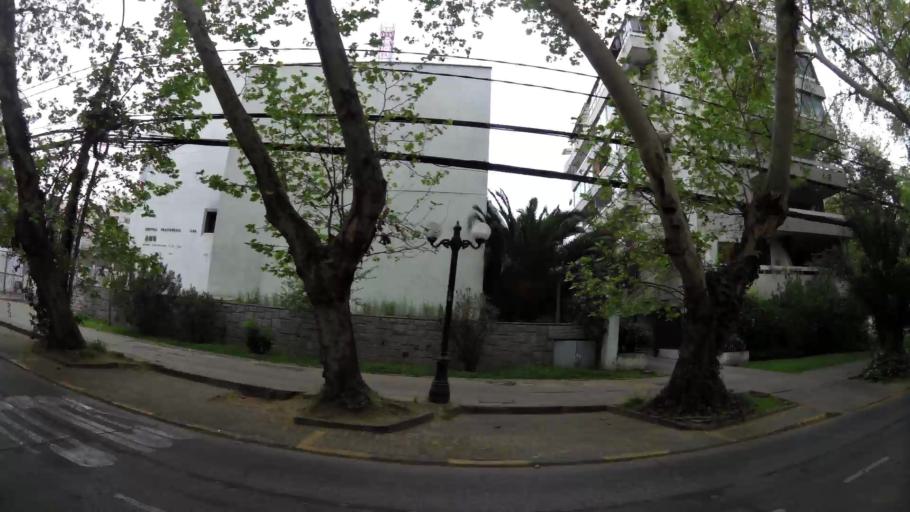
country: CL
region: Santiago Metropolitan
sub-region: Provincia de Santiago
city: Villa Presidente Frei, Nunoa, Santiago, Chile
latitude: -33.4225
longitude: -70.6028
